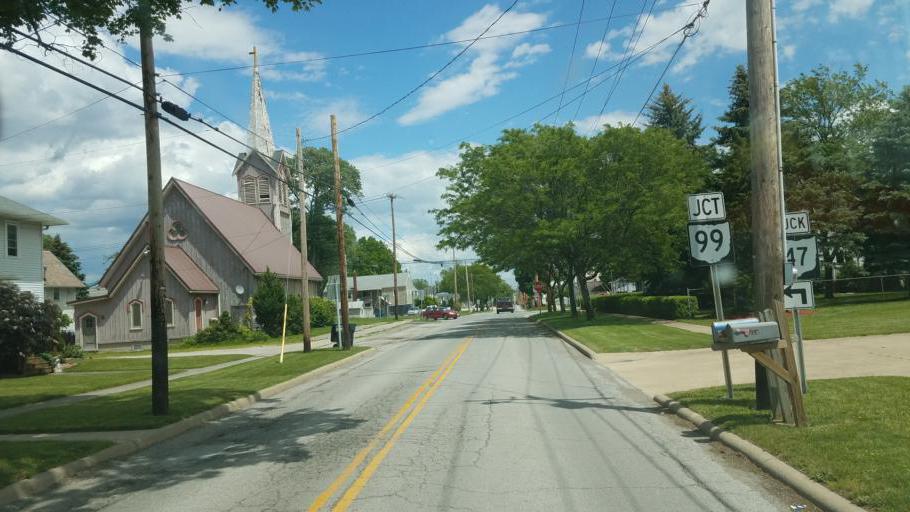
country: US
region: Ohio
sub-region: Huron County
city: Monroeville
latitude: 41.2426
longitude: -82.7042
